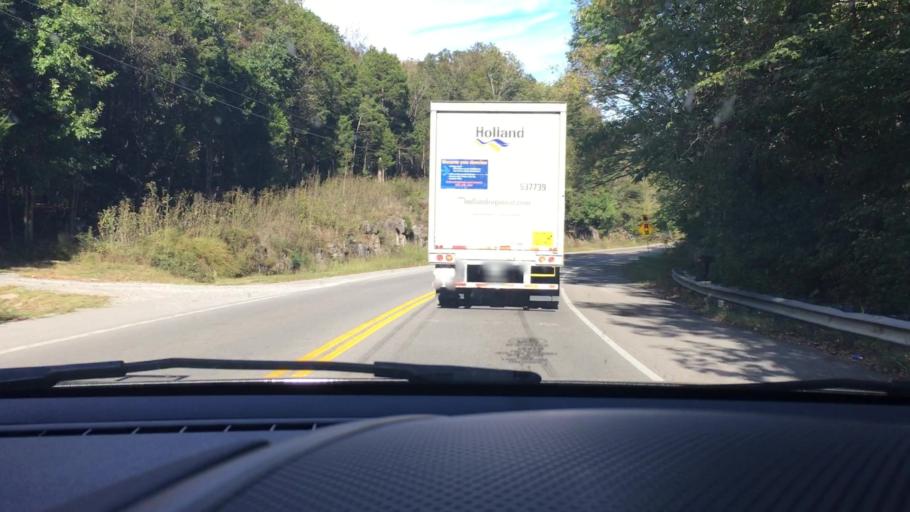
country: US
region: Tennessee
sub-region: Montgomery County
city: Clarksville
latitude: 36.4727
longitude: -87.3801
